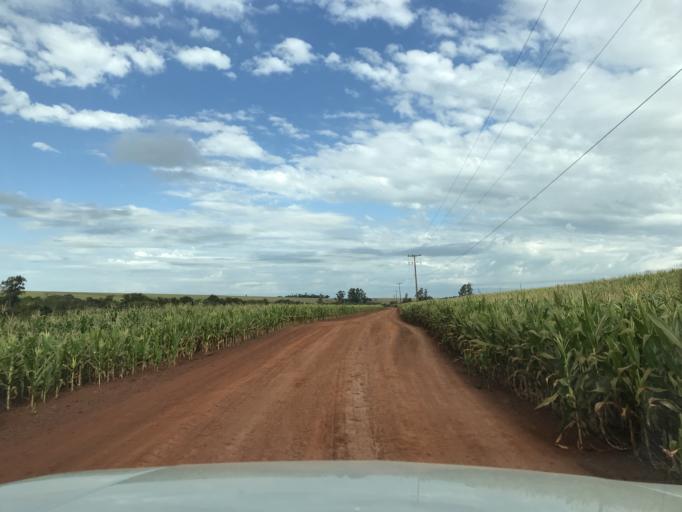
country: BR
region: Parana
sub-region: Palotina
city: Palotina
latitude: -24.3153
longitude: -53.8071
